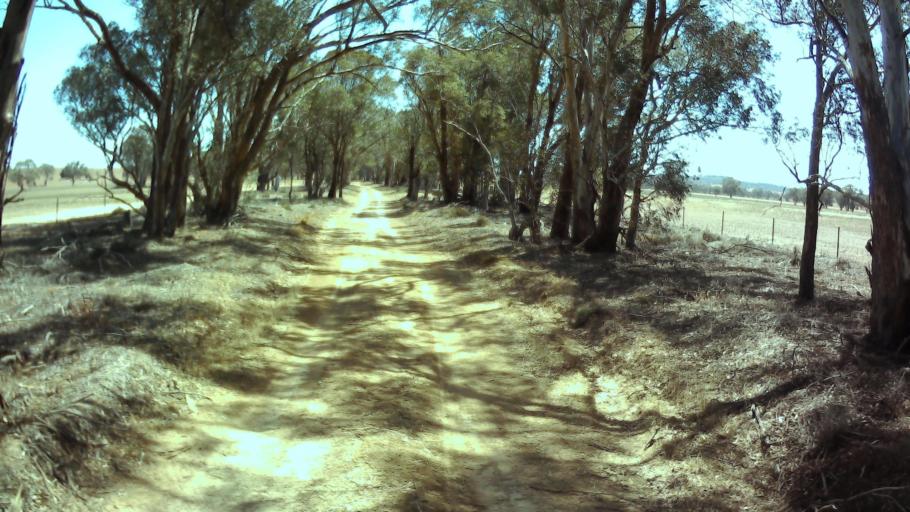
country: AU
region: New South Wales
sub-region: Weddin
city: Grenfell
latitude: -33.9904
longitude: 148.1640
